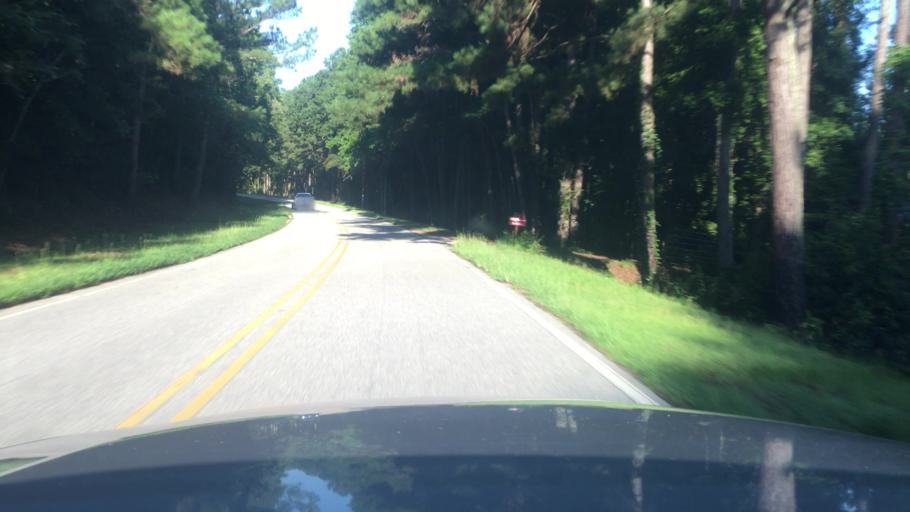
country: US
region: North Carolina
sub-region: Harnett County
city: Walkertown
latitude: 35.2270
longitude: -78.8854
